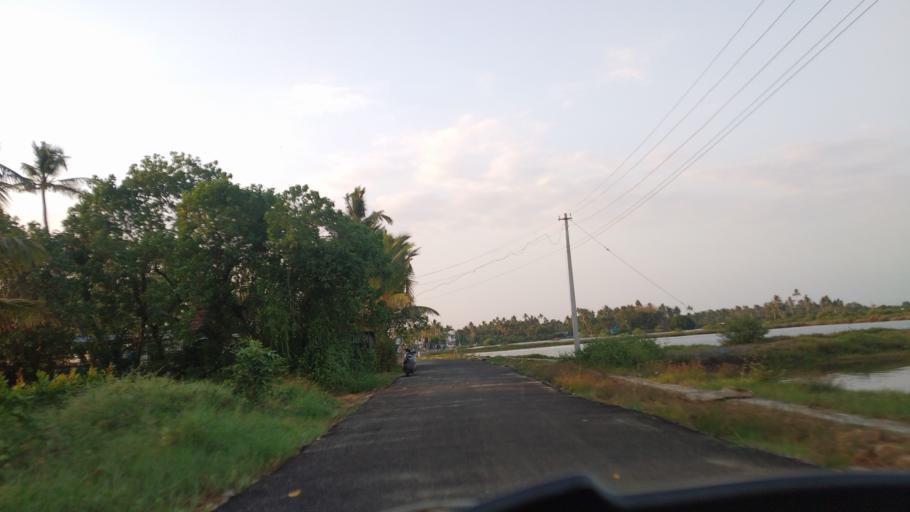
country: IN
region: Kerala
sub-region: Ernakulam
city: Elur
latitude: 10.0507
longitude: 76.2268
